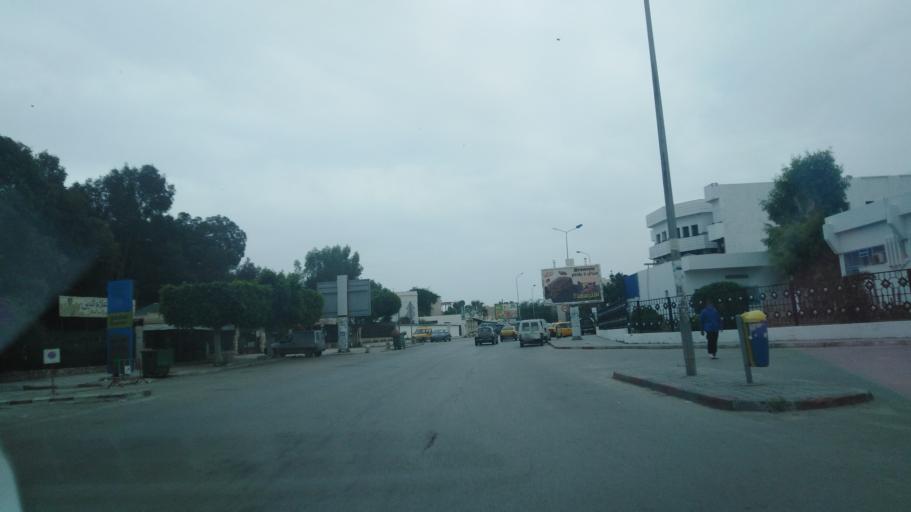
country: TN
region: Susah
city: Sousse
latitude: 35.8304
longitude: 10.6288
